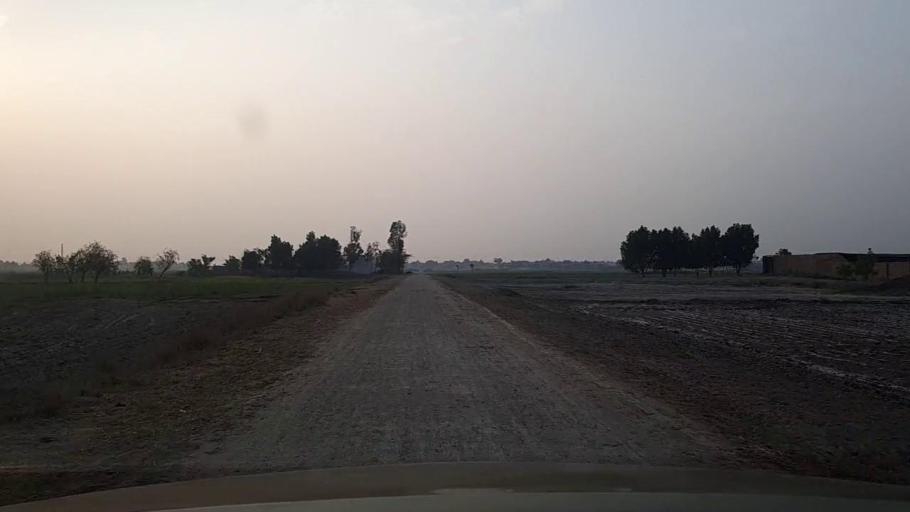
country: PK
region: Sindh
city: Sanghar
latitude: 26.1858
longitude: 68.9463
